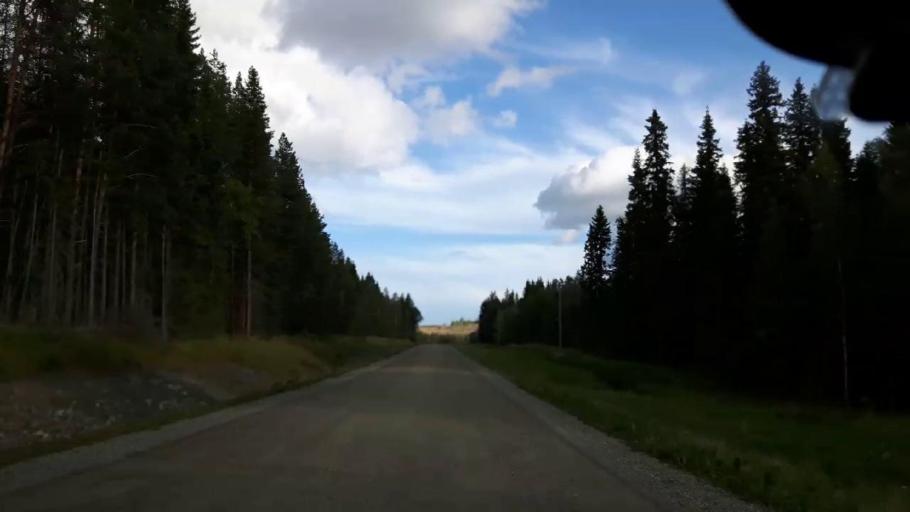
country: SE
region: Jaemtland
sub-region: Stroemsunds Kommun
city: Stroemsund
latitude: 63.3013
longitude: 15.5775
